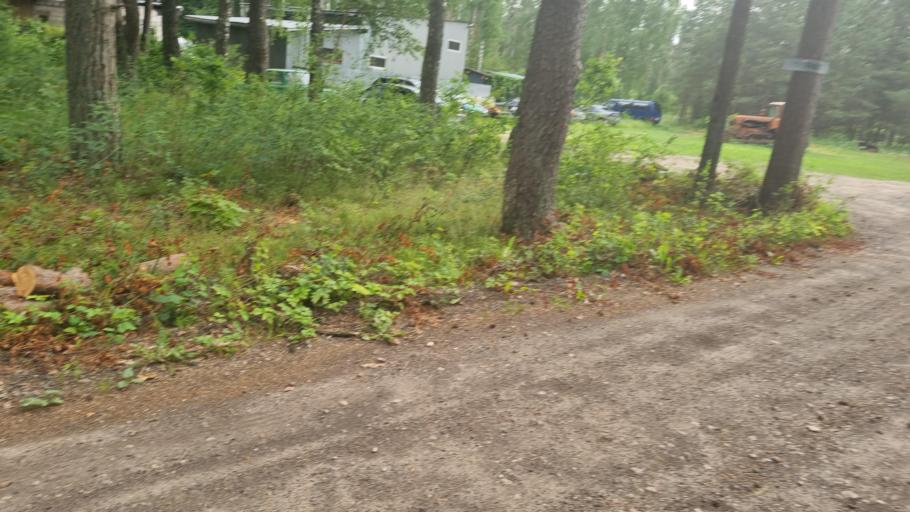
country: LV
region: Kekava
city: Balozi
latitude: 56.8911
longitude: 24.1276
